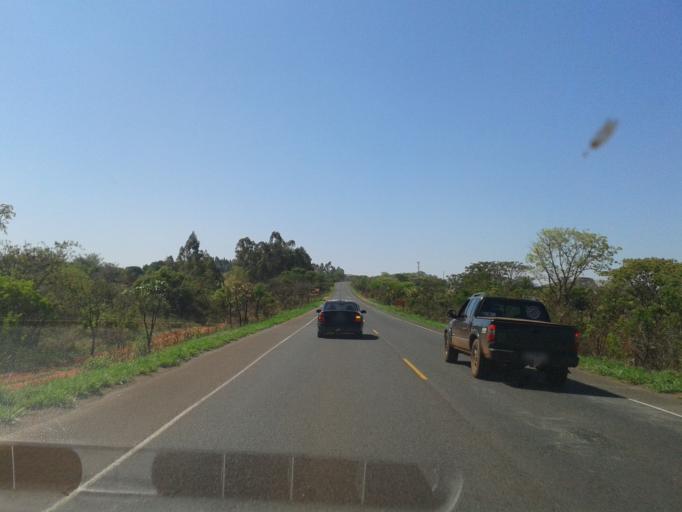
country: BR
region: Minas Gerais
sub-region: Uberlandia
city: Uberlandia
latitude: -19.0495
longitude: -48.0464
